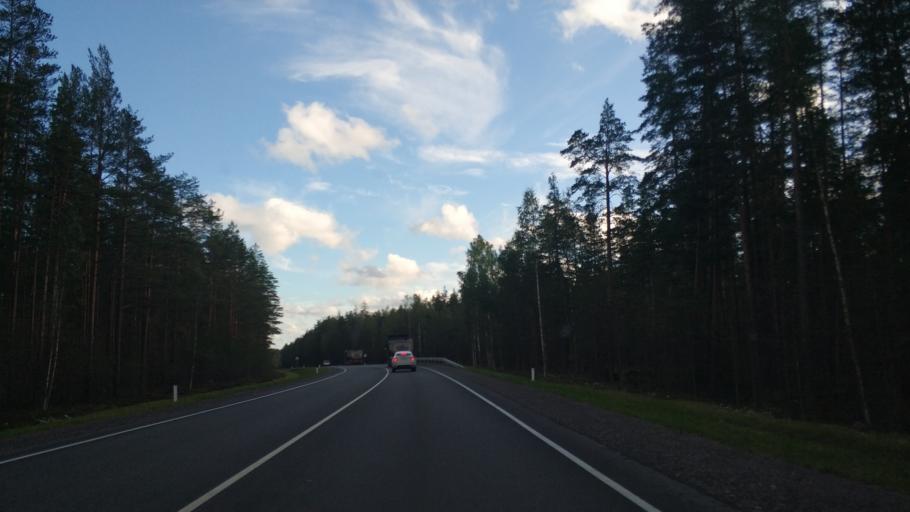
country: RU
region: Leningrad
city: Priozersk
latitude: 60.8819
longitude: 30.1606
